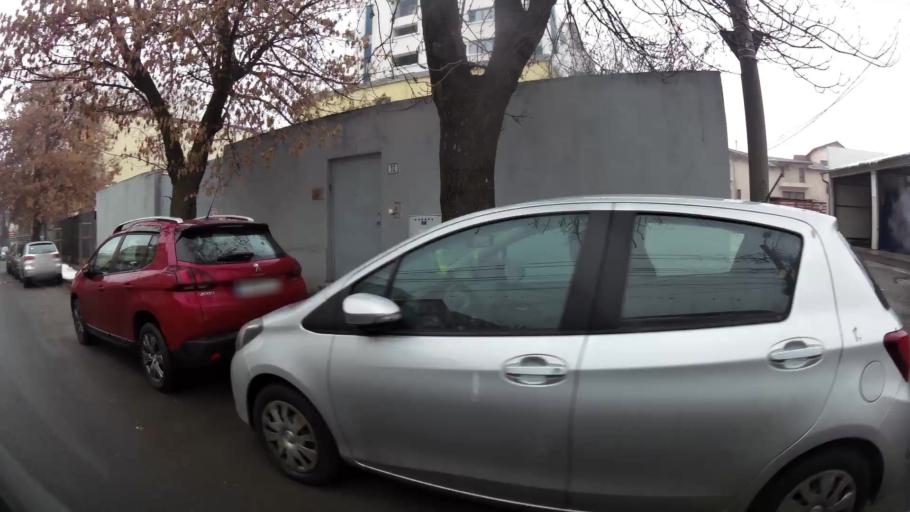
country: RO
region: Ilfov
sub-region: Comuna Chiajna
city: Rosu
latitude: 44.4447
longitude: 26.0335
